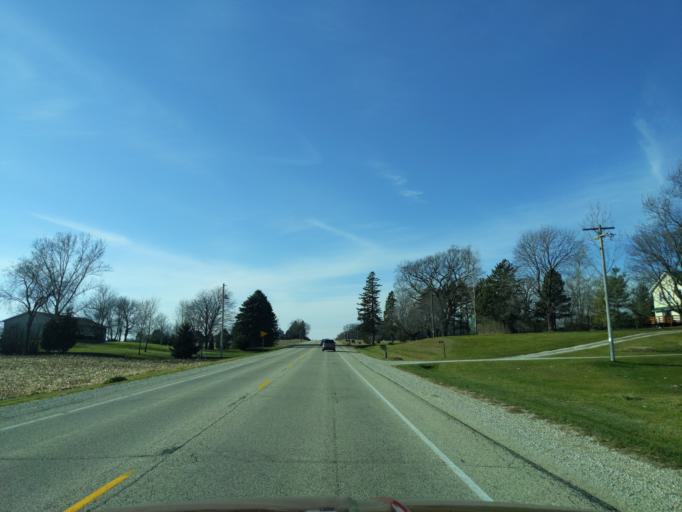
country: US
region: Wisconsin
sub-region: Jefferson County
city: Fort Atkinson
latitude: 42.8294
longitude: -88.8504
